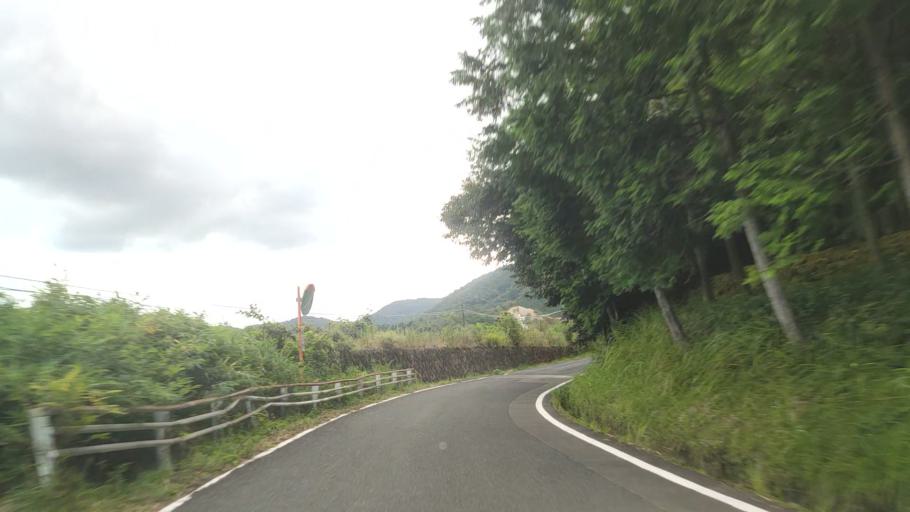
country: JP
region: Hyogo
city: Toyooka
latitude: 35.6000
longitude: 134.8876
